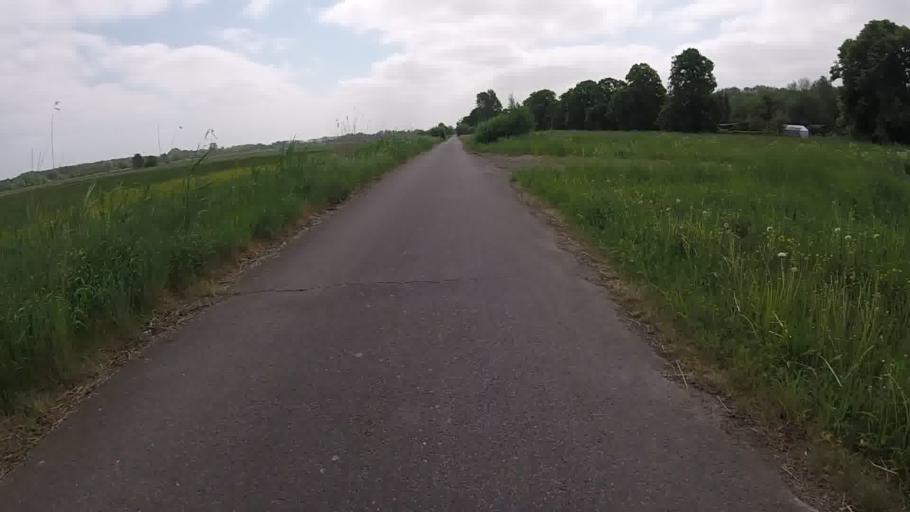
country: DE
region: Hamburg
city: Wandsbek
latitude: 53.5070
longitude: 10.1162
